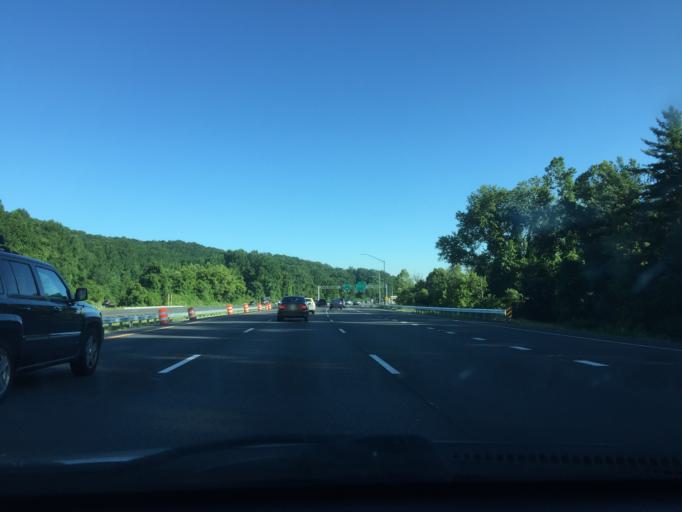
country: US
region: Maryland
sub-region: Baltimore County
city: Cockeysville
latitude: 39.4634
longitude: -76.6594
